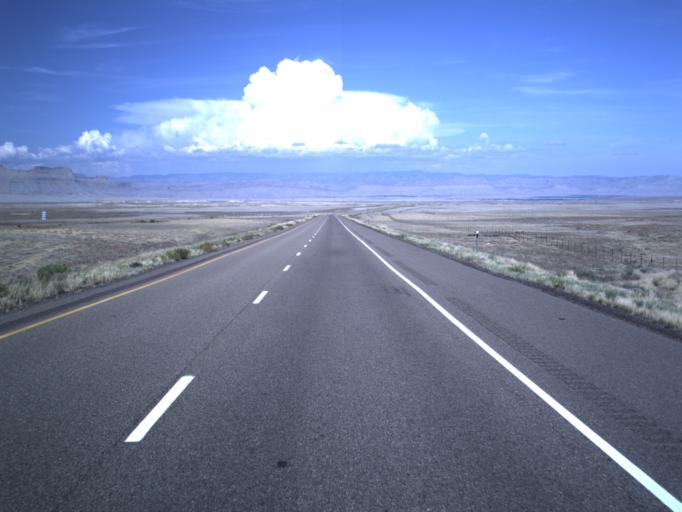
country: US
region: Utah
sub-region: Carbon County
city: East Carbon City
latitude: 38.9446
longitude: -110.3266
